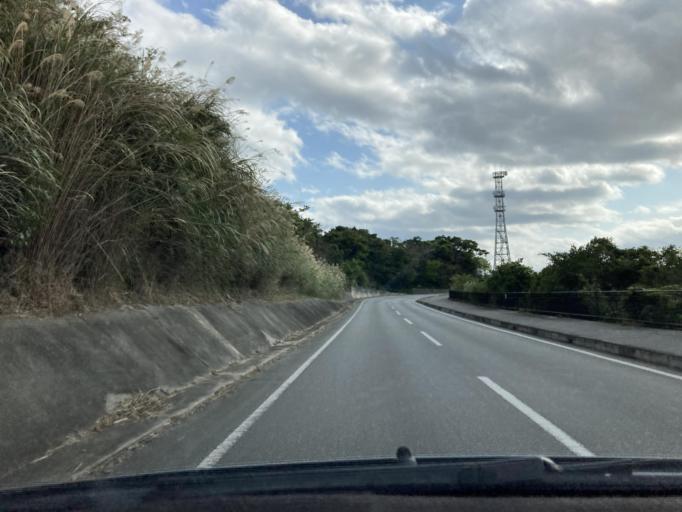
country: JP
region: Okinawa
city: Tomigusuku
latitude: 26.1728
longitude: 127.7602
